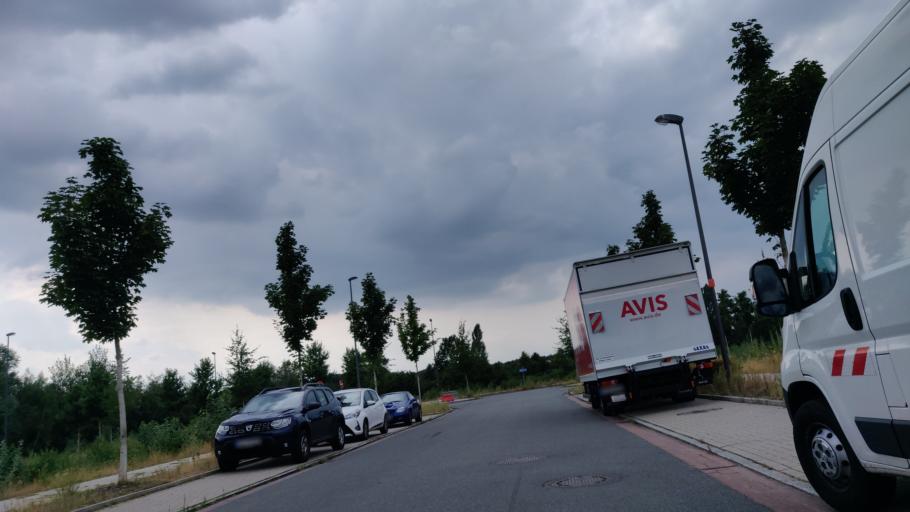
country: DE
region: Bremen
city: Bremen
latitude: 53.1020
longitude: 8.8487
